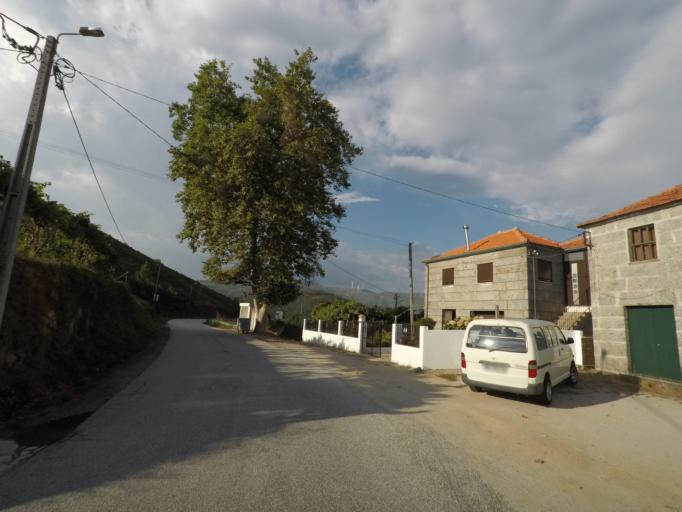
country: PT
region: Porto
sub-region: Baiao
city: Valadares
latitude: 41.1782
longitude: -7.9351
